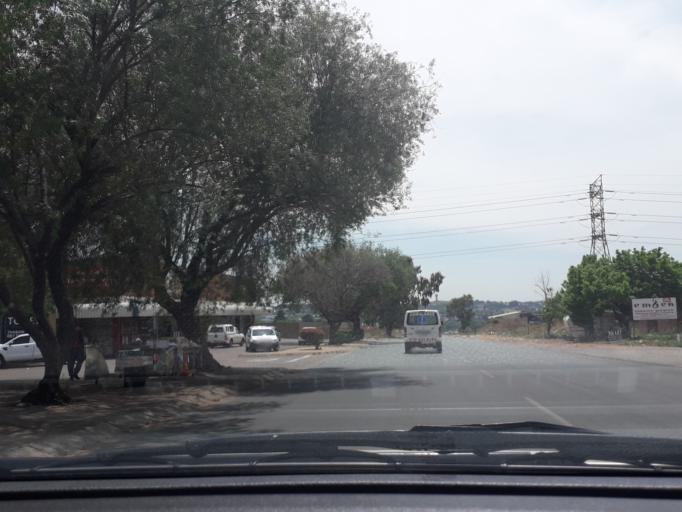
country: ZA
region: Gauteng
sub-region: City of Johannesburg Metropolitan Municipality
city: Roodepoort
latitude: -26.1905
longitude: 27.9240
